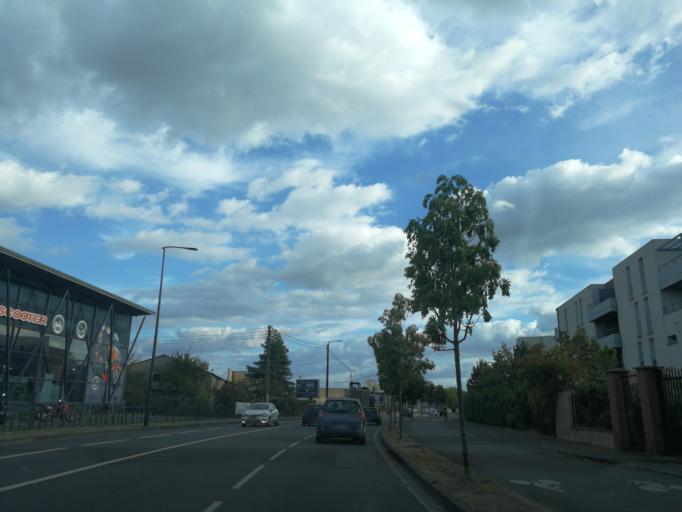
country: FR
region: Midi-Pyrenees
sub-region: Departement de la Haute-Garonne
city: L'Union
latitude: 43.6379
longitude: 1.4720
